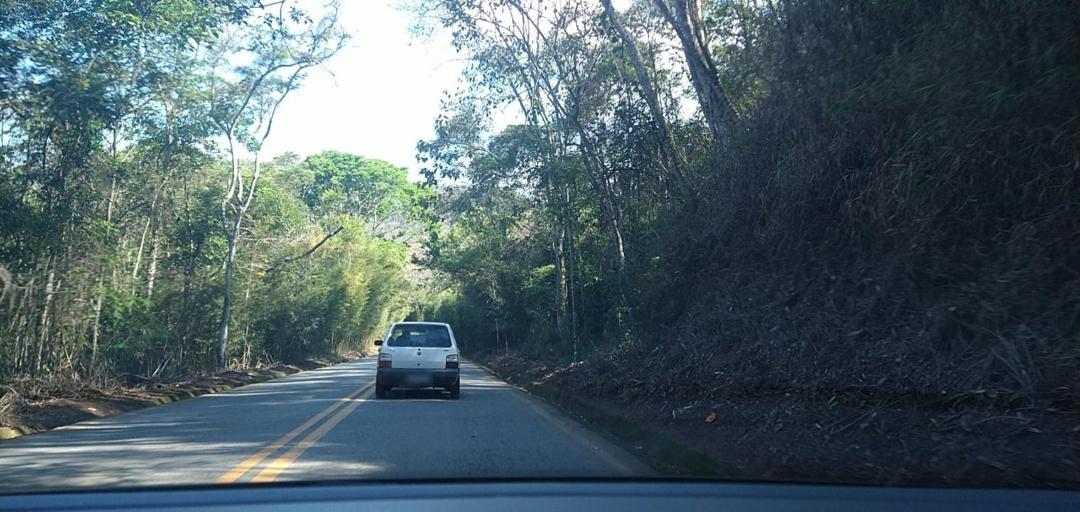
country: BR
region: Minas Gerais
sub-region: Alvinopolis
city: Alvinopolis
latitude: -20.0380
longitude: -43.0327
